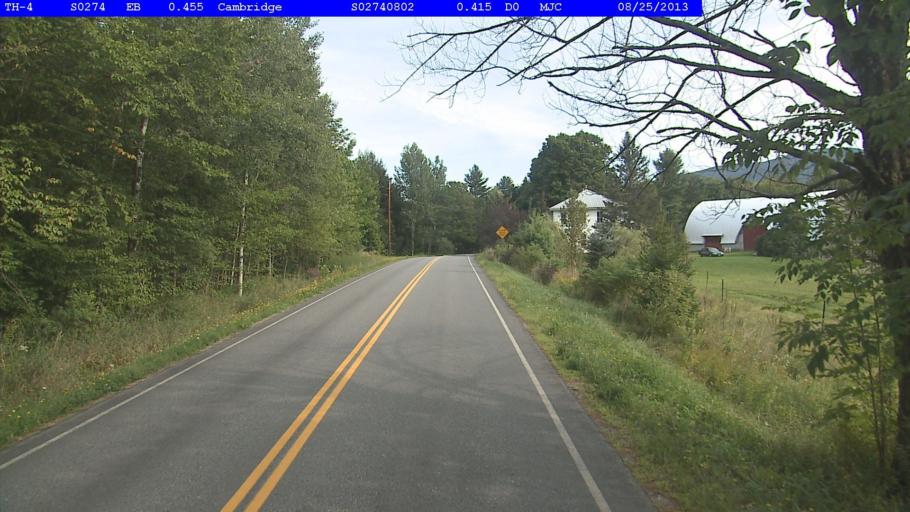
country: US
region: Vermont
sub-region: Lamoille County
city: Johnson
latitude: 44.6769
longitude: -72.7697
